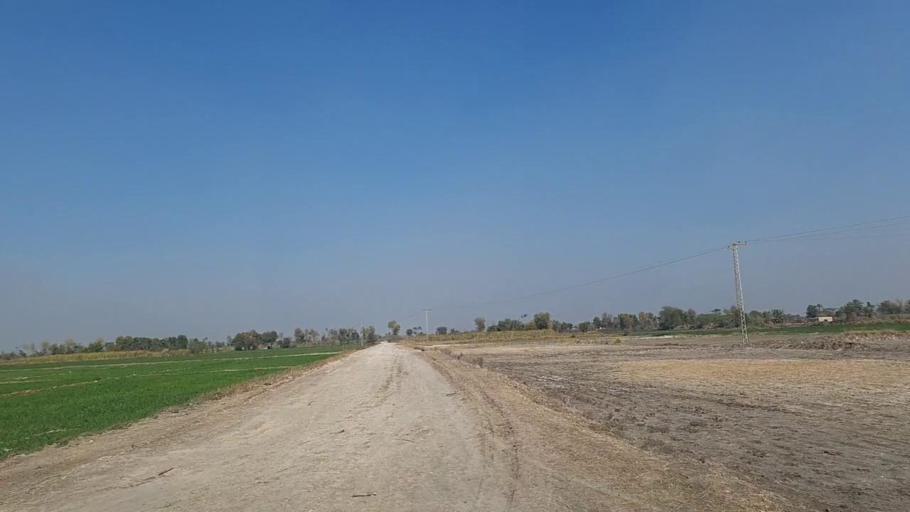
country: PK
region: Sindh
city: Daur
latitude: 26.4854
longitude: 68.3384
